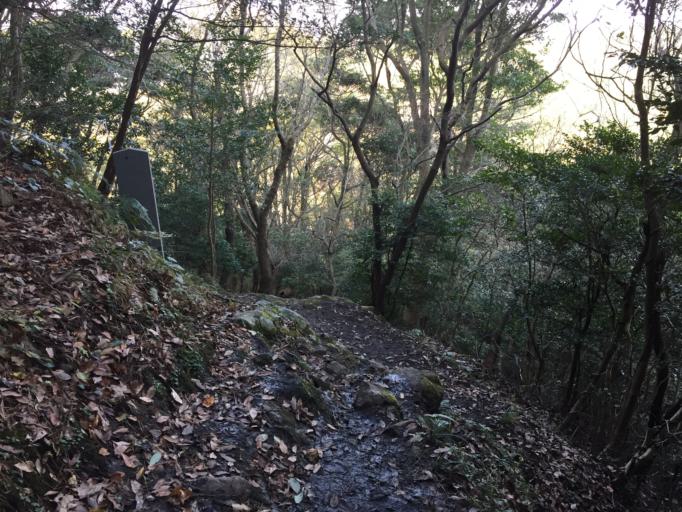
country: JP
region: Oita
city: Bungo-Takada-shi
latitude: 33.6267
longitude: 131.6042
